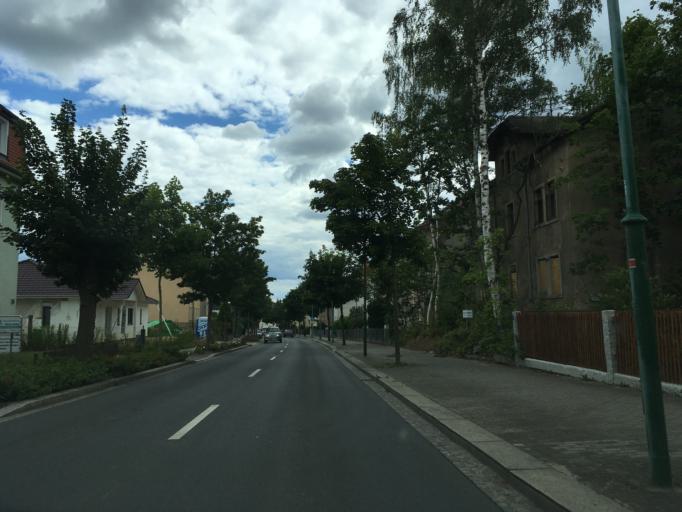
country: DE
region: Saxony
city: Radeberg
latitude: 51.1264
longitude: 13.9163
